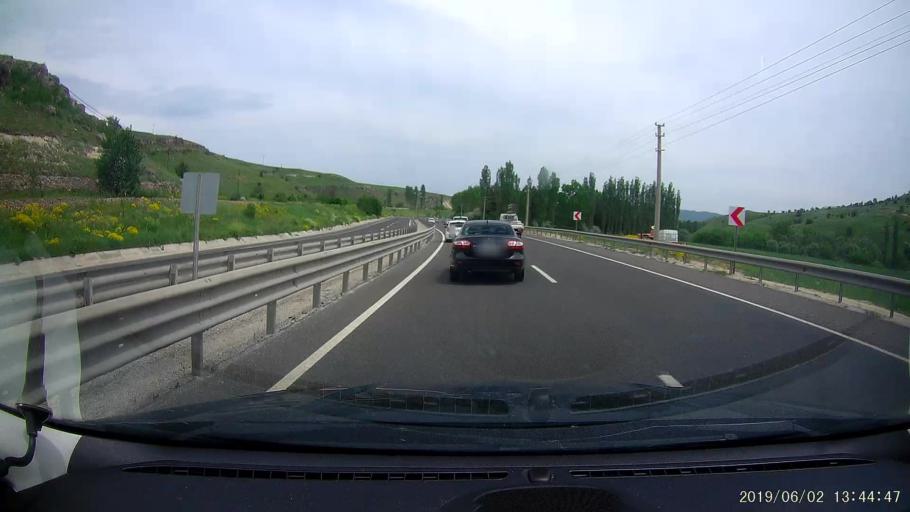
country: TR
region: Cankiri
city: Kursunlu
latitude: 40.8475
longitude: 33.2377
